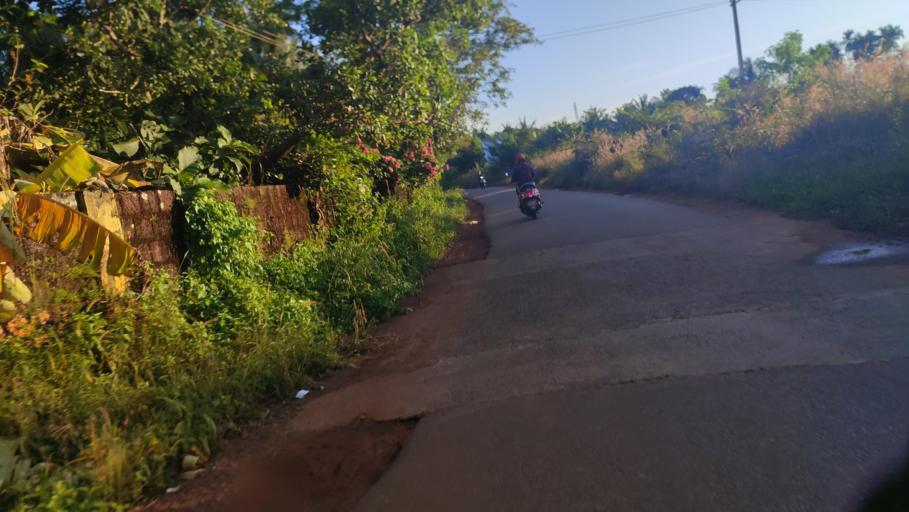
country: IN
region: Kerala
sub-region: Kasaragod District
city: Kannangad
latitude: 12.4143
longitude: 75.0950
